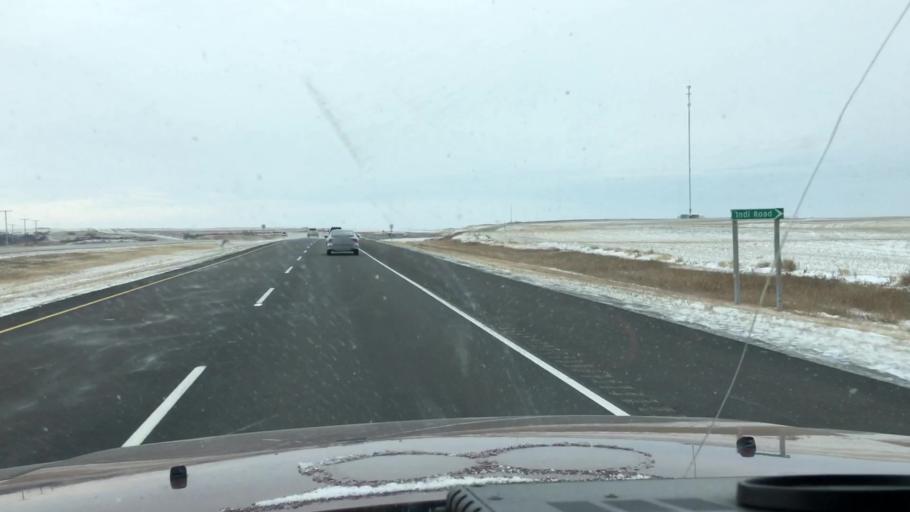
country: CA
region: Saskatchewan
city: Saskatoon
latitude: 51.7417
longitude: -106.4763
